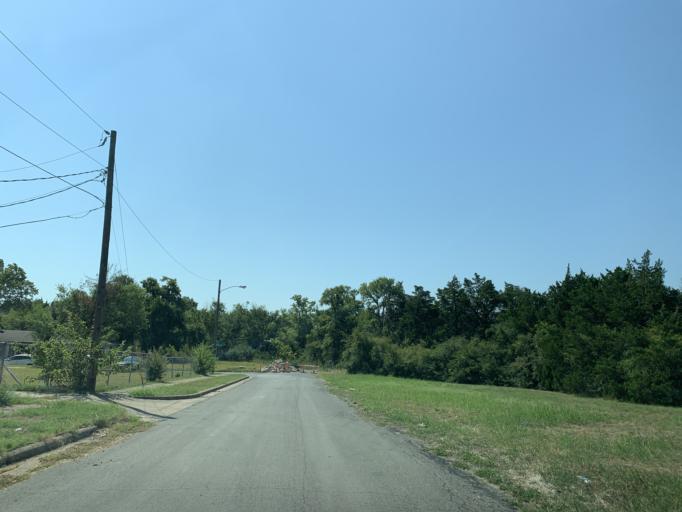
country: US
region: Texas
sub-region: Dallas County
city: Hutchins
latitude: 32.6590
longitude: -96.7587
